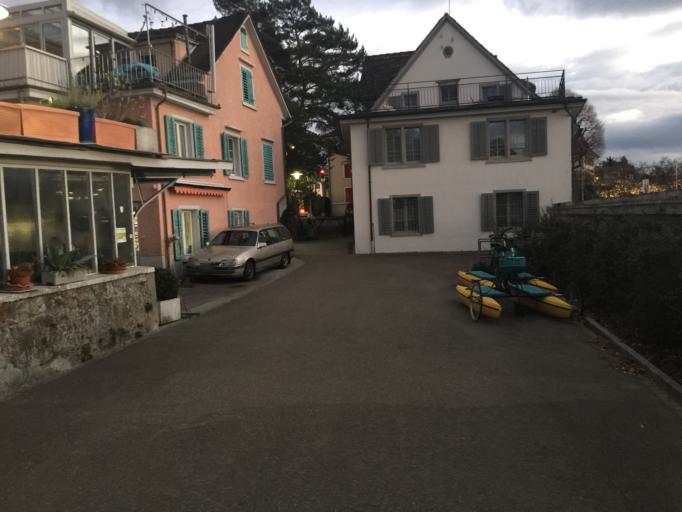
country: CH
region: Zurich
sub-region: Bezirk Meilen
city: Kuesnacht / Dorf
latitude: 47.3201
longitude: 8.5785
